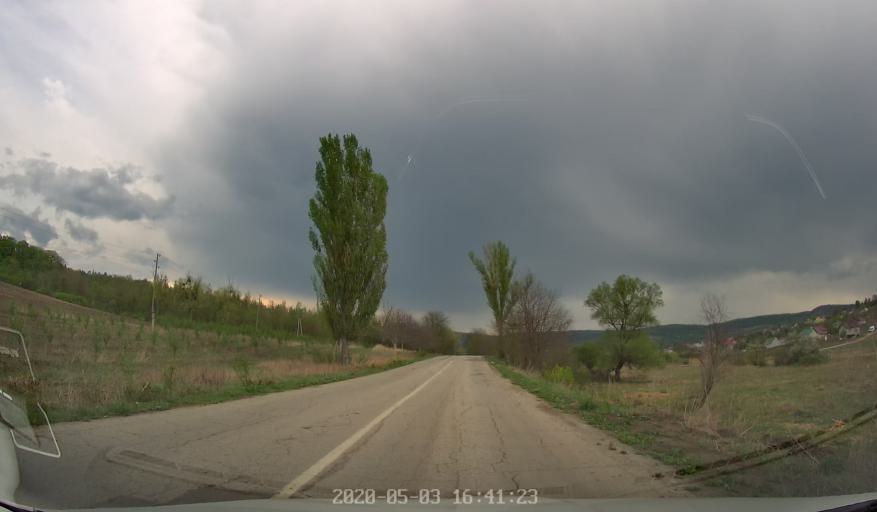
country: MD
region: Stinga Nistrului
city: Bucovat
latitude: 47.1674
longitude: 28.4076
